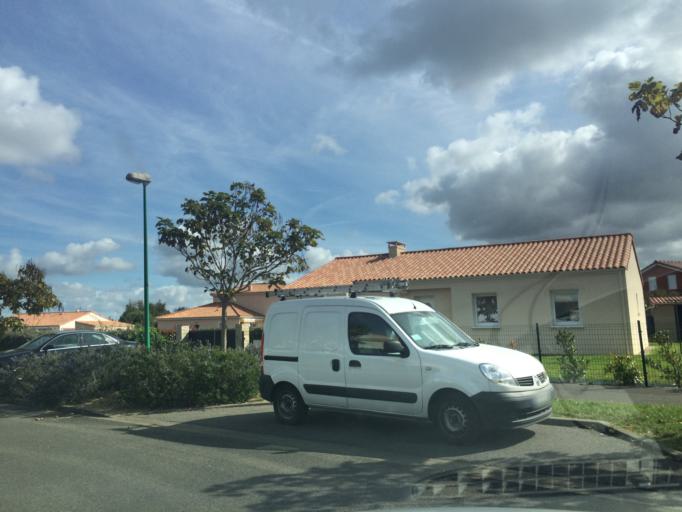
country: FR
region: Pays de la Loire
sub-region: Departement de la Loire-Atlantique
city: Chemere
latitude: 47.1140
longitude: -1.9184
